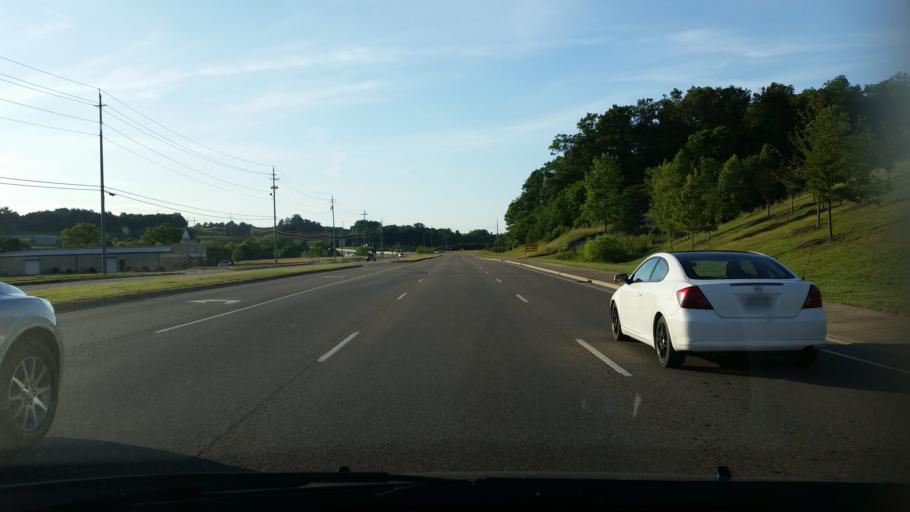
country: US
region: Tennessee
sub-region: Sevier County
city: Pigeon Forge
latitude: 35.8131
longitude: -83.5374
